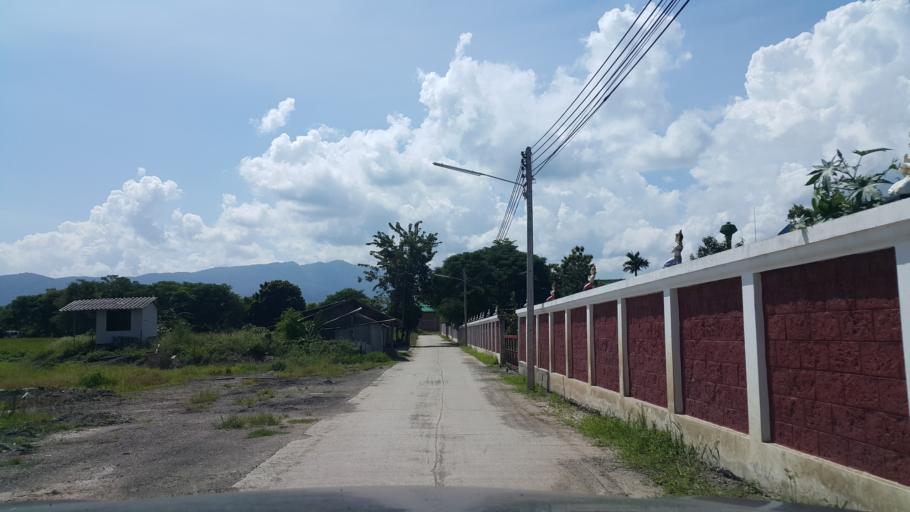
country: TH
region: Chiang Mai
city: Chom Thong
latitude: 18.4198
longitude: 98.6830
